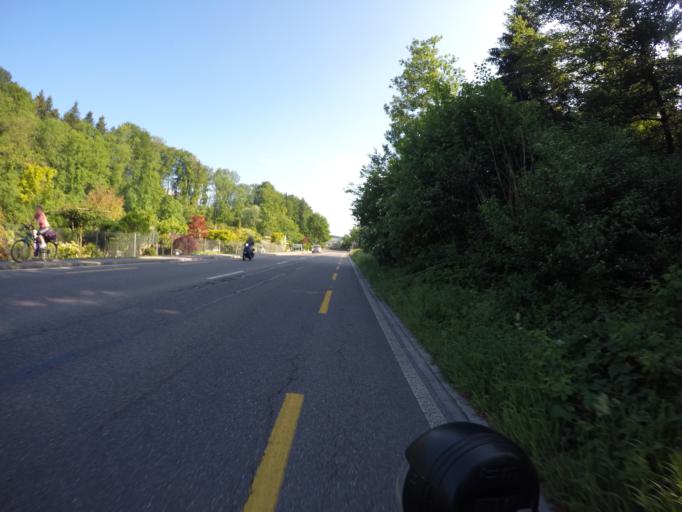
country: CH
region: Zurich
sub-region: Bezirk Winterthur
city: Toss
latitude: 47.4714
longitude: 8.7043
